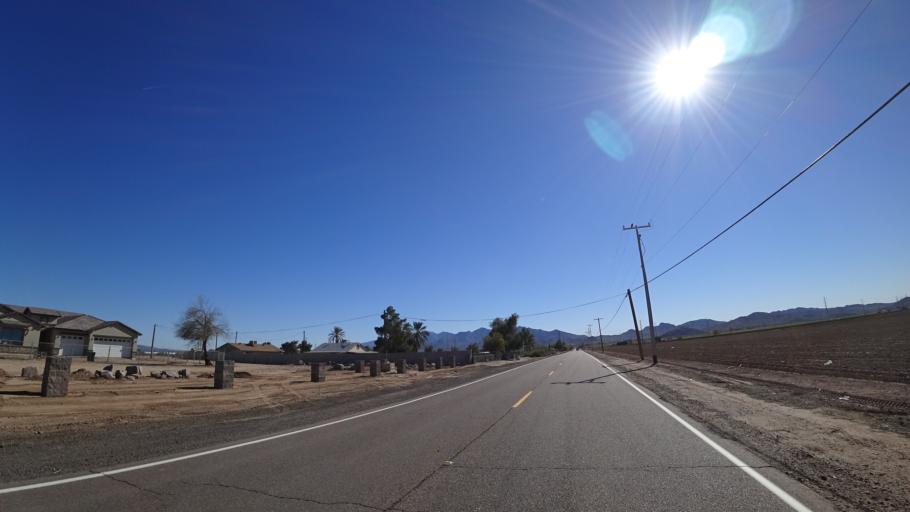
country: US
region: Arizona
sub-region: Maricopa County
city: Goodyear
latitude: 33.4127
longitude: -112.3576
